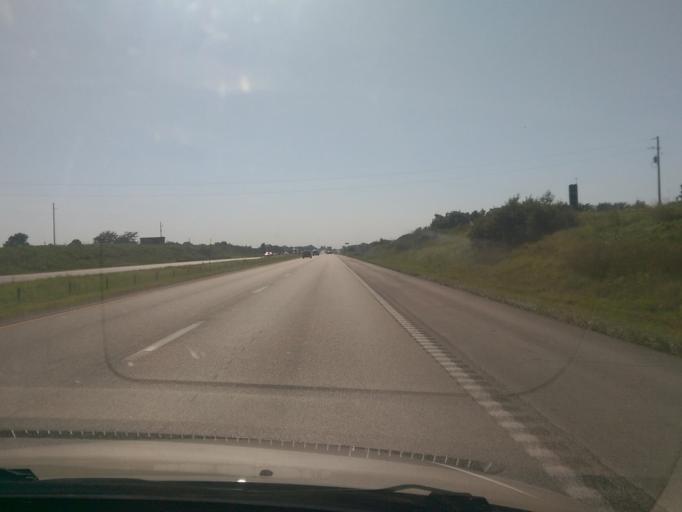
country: US
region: Missouri
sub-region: Saline County
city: Sweet Springs
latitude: 38.9741
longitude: -93.3472
